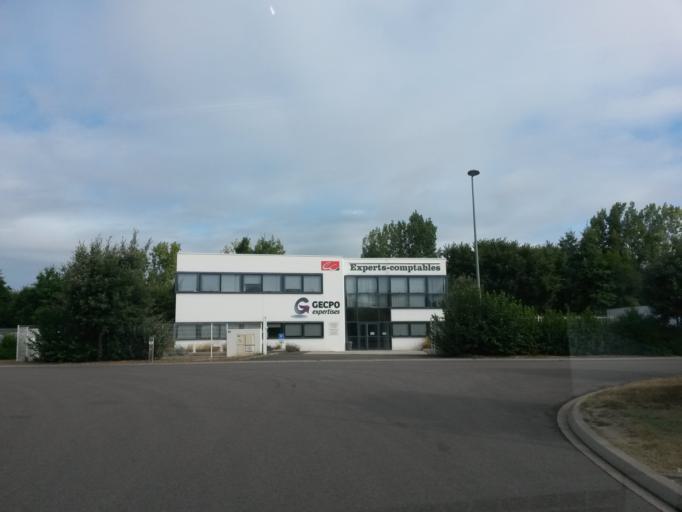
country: FR
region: Pays de la Loire
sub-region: Departement de la Vendee
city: Les Sables-d'Olonne
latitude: 46.5171
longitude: -1.7854
